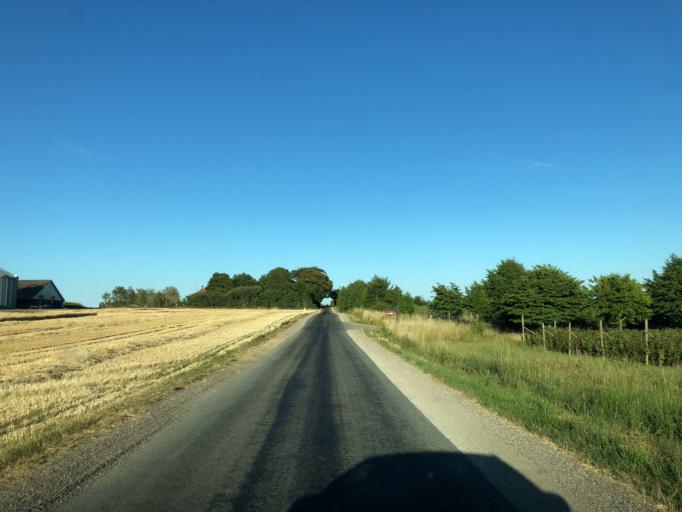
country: DK
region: Central Jutland
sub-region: Horsens Kommune
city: Horsens
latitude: 55.9220
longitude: 9.8794
